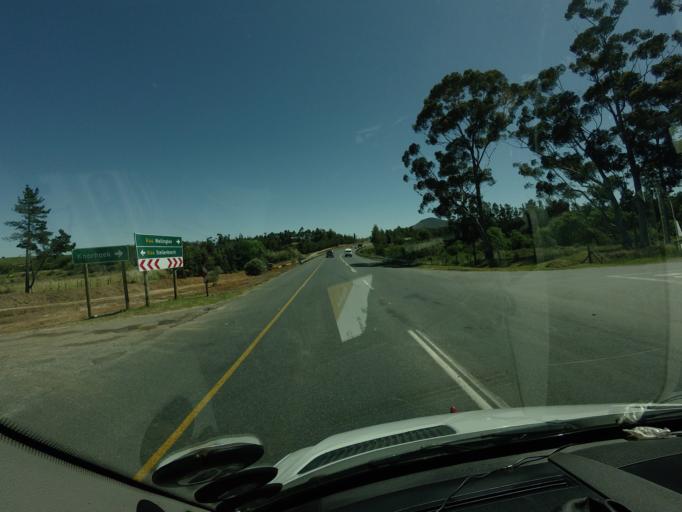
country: ZA
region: Western Cape
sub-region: Cape Winelands District Municipality
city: Stellenbosch
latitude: -33.8706
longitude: 18.8488
